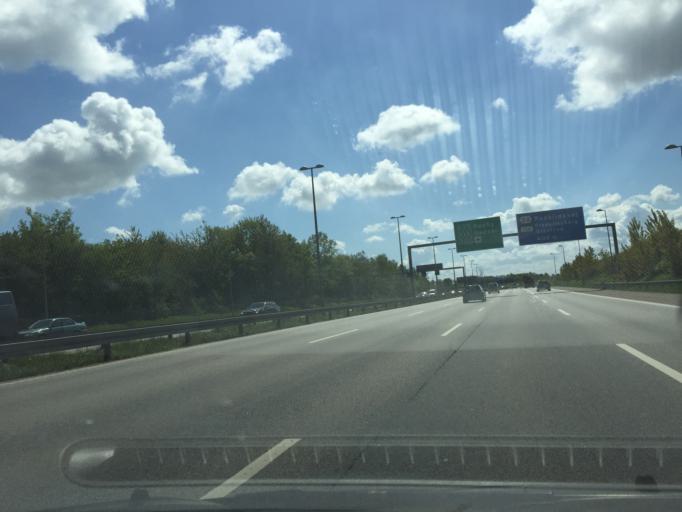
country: DK
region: Capital Region
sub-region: Glostrup Kommune
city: Glostrup
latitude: 55.6776
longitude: 12.4255
